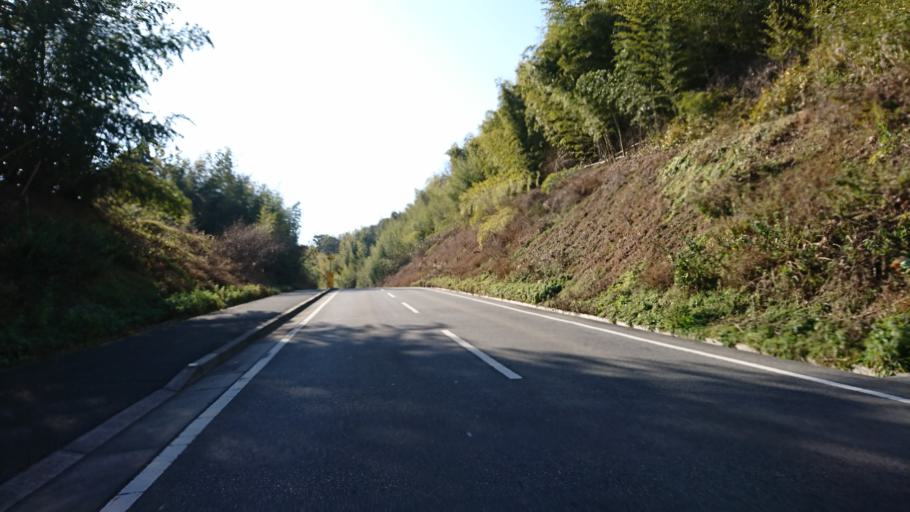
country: JP
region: Hyogo
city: Kakogawacho-honmachi
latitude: 34.8262
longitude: 134.8279
